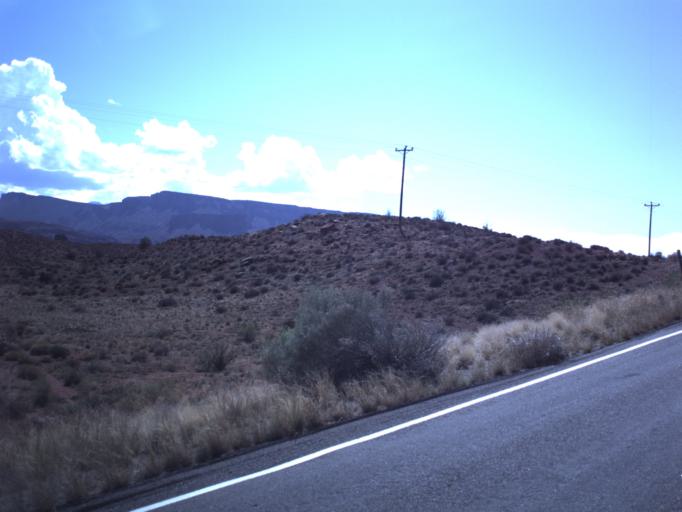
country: US
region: Utah
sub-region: Grand County
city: Moab
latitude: 38.7542
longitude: -109.3281
